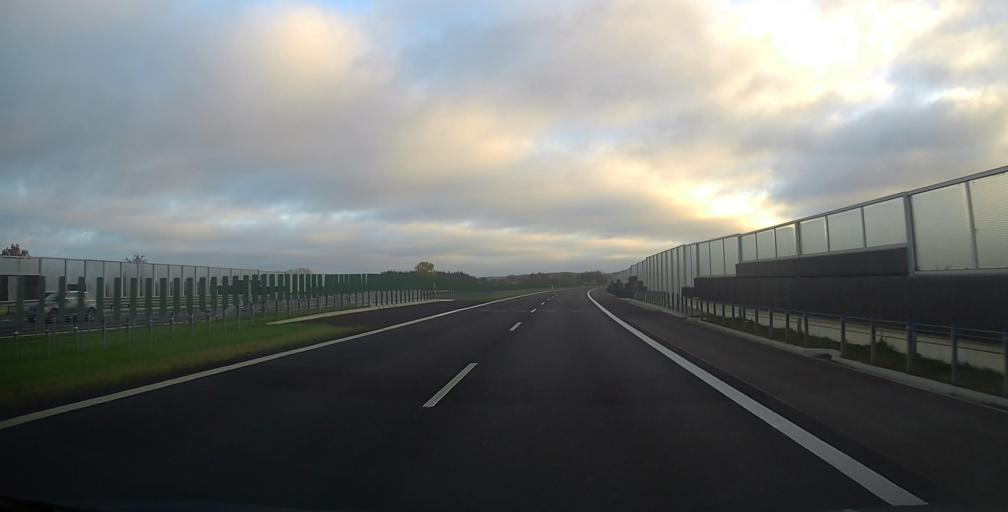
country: PL
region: Podlasie
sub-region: Powiat grajewski
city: Szczuczyn
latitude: 53.5730
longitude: 22.2783
